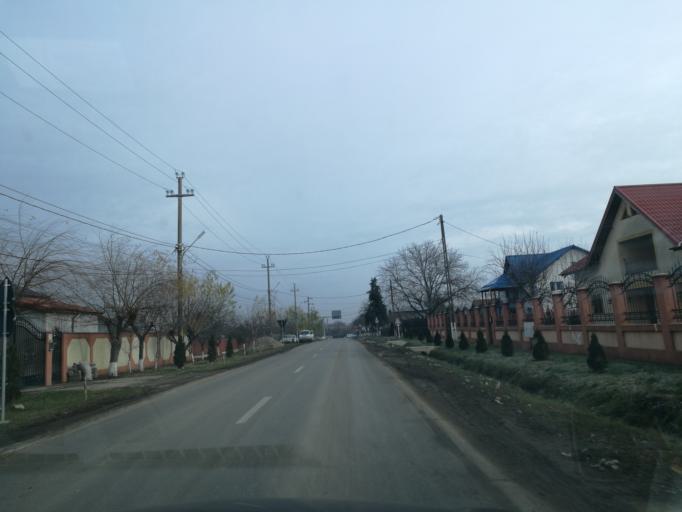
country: RO
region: Ilfov
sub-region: Comuna Moara Vlasiei
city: Moara Vlasiei
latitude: 44.6357
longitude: 26.1915
